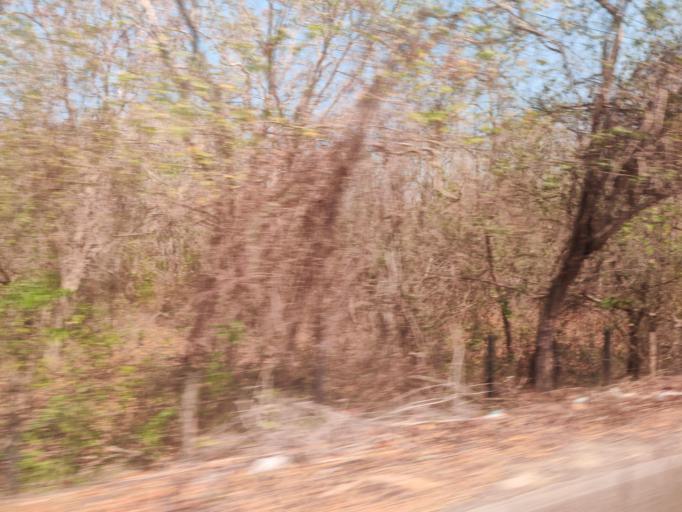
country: CO
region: Bolivar
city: Turbana
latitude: 10.2190
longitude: -75.5860
